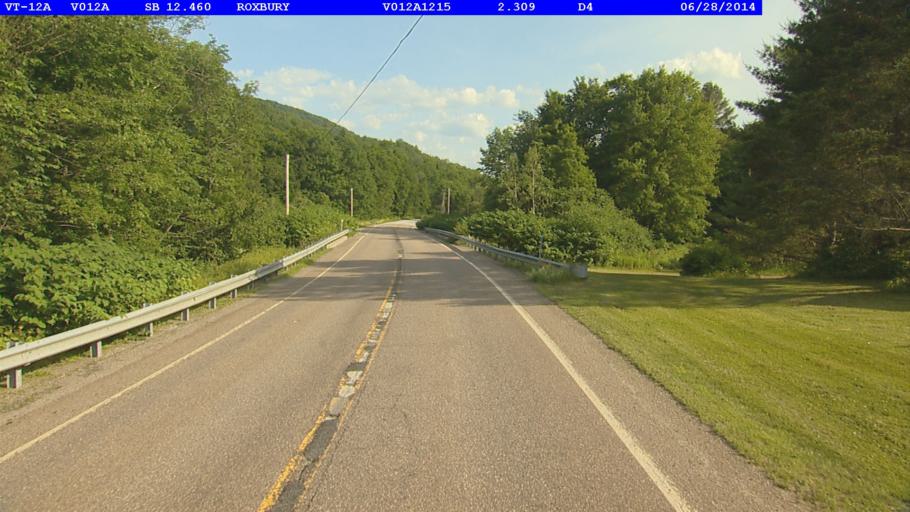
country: US
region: Vermont
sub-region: Washington County
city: Northfield
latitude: 44.0618
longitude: -72.7432
